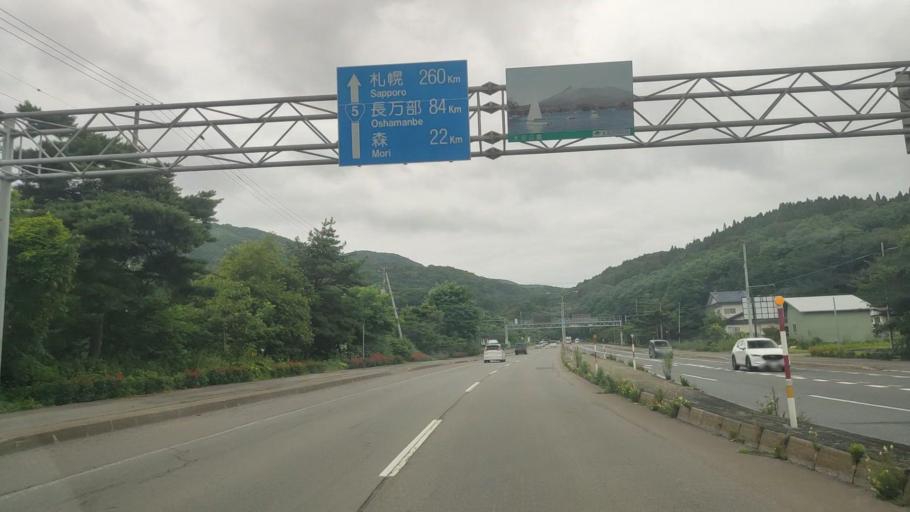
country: JP
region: Hokkaido
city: Nanae
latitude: 41.9301
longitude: 140.6427
